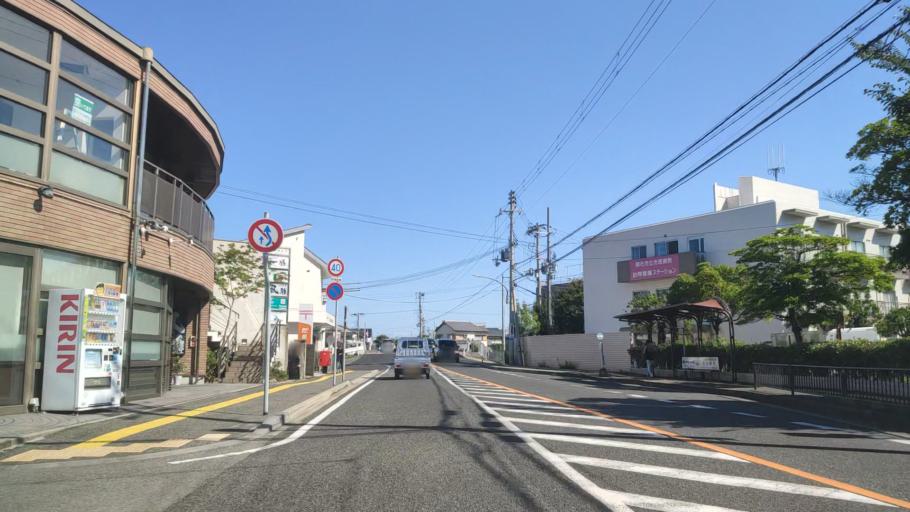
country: JP
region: Hyogo
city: Akashi
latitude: 34.6573
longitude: 134.9894
